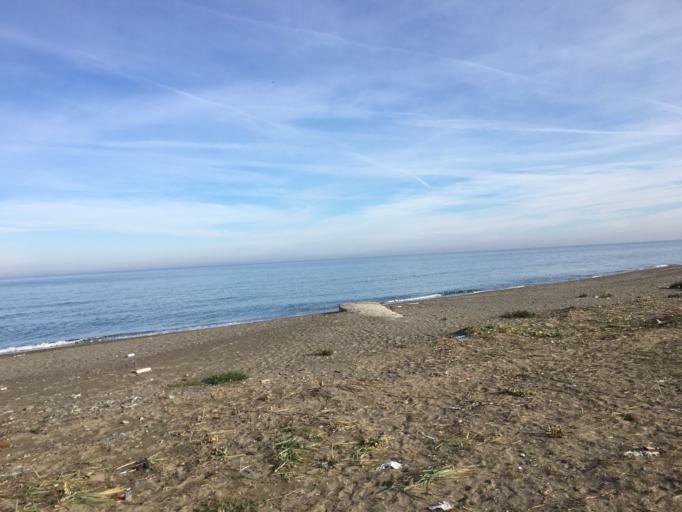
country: TR
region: Samsun
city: Alacam
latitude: 41.6349
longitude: 35.6105
